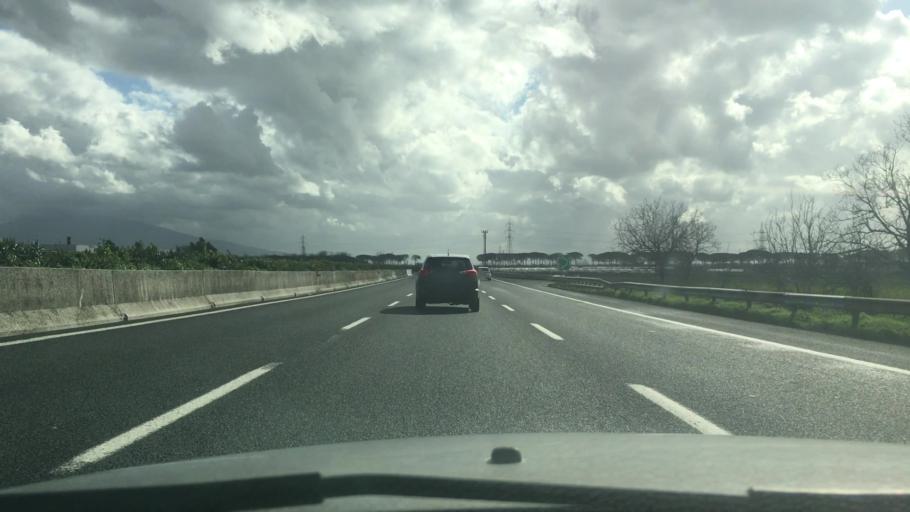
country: IT
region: Campania
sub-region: Provincia di Napoli
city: Pascarola
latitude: 40.9965
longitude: 14.3242
